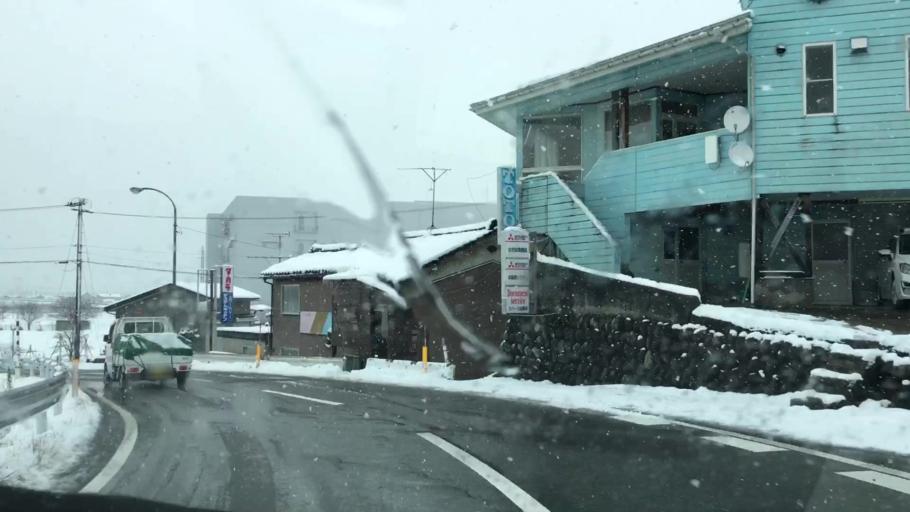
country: JP
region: Toyama
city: Kamiichi
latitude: 36.6968
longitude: 137.3380
